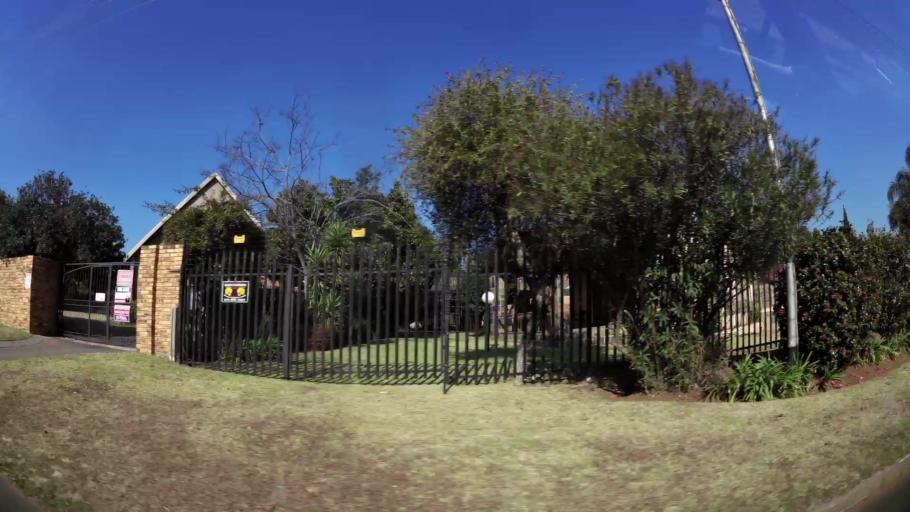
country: ZA
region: Gauteng
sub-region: West Rand District Municipality
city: Randfontein
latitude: -26.1594
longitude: 27.6944
